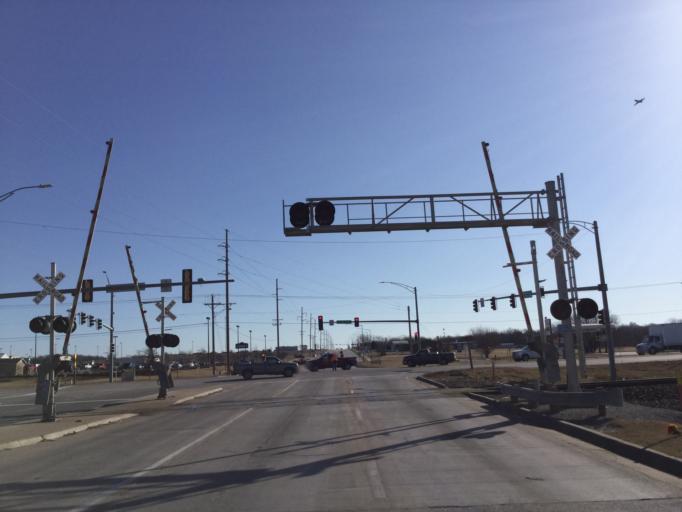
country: US
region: Kansas
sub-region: Sedgwick County
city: Derby
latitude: 37.5769
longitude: -97.2809
